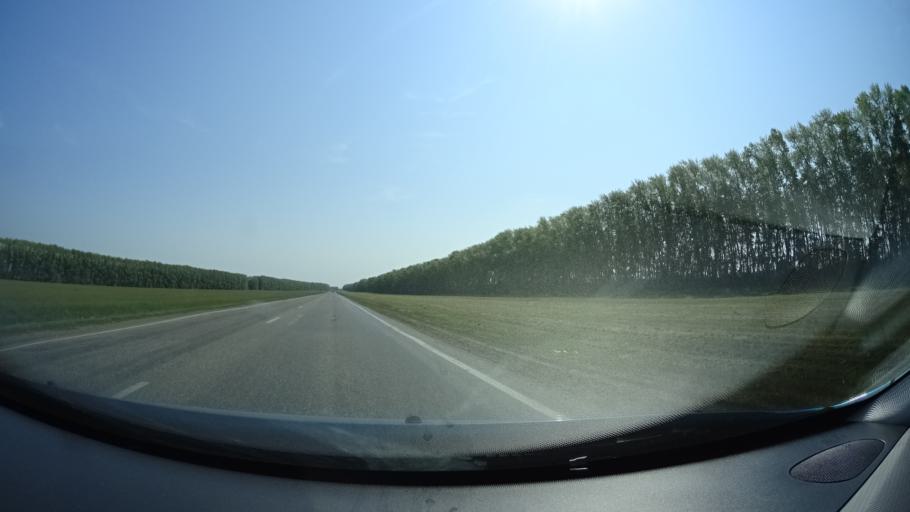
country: RU
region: Bashkortostan
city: Karmaskaly
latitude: 54.3969
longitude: 56.1042
